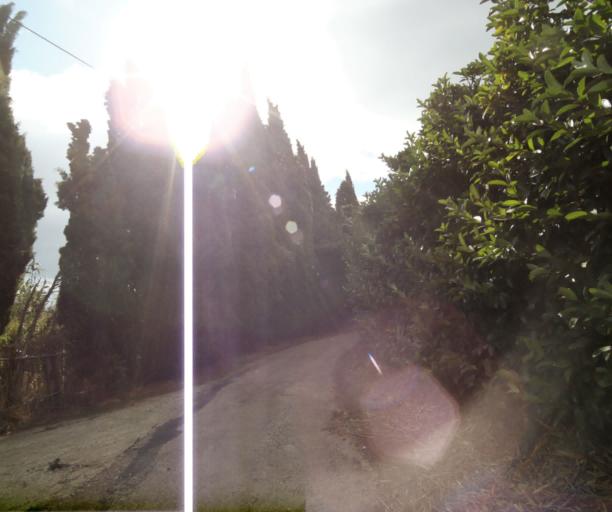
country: FR
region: Languedoc-Roussillon
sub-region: Departement des Pyrenees-Orientales
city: Argelers
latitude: 42.5807
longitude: 3.0248
